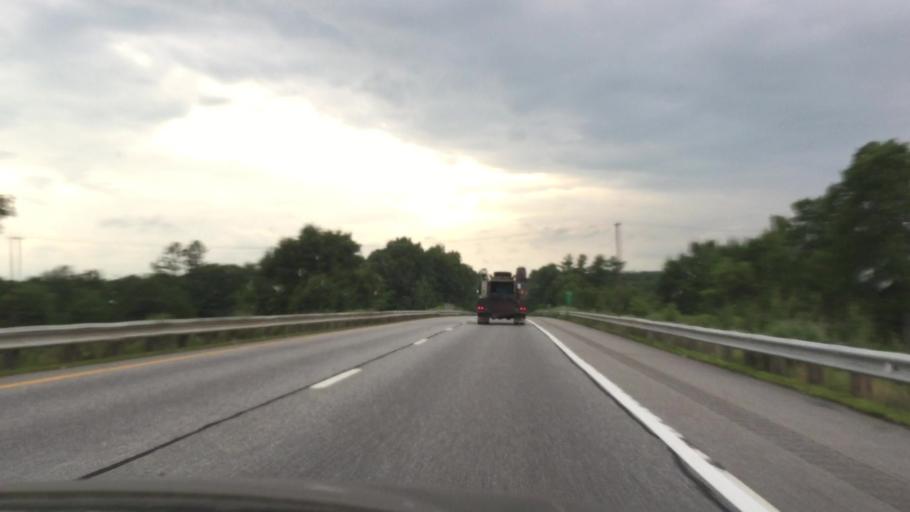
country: US
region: New Hampshire
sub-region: Merrimack County
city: East Concord
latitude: 43.2730
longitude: -71.5605
